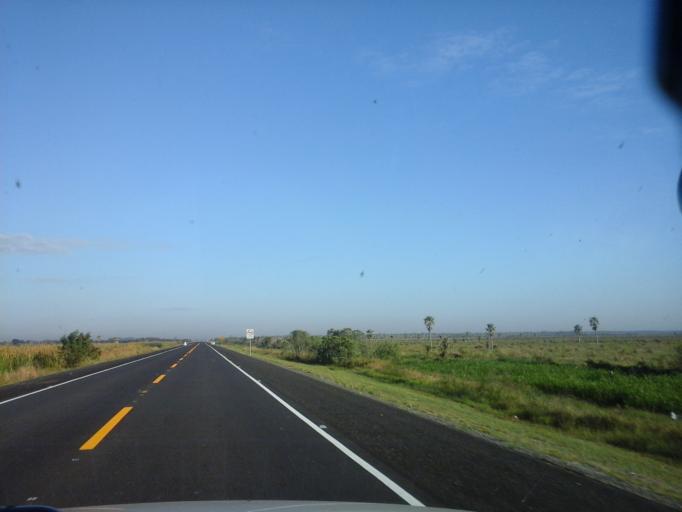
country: PY
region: Neembucu
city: Pilar
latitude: -26.8648
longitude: -57.8329
